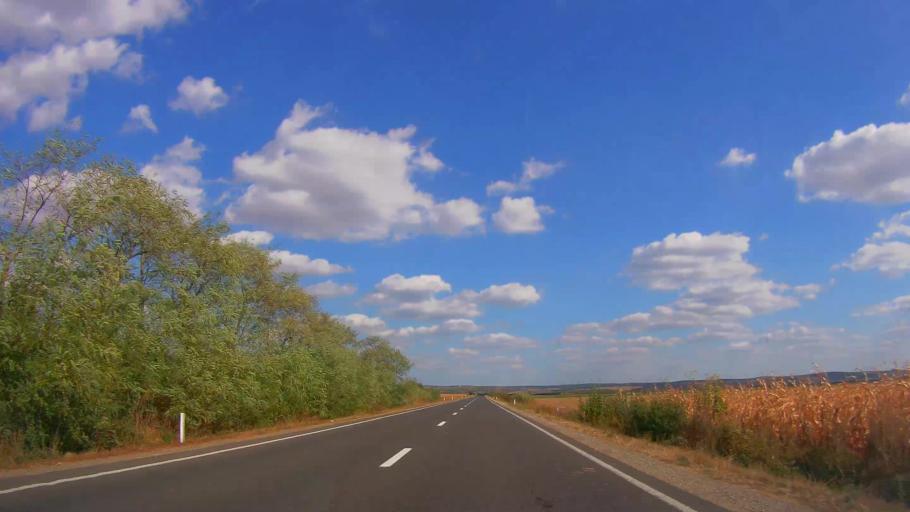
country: RO
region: Satu Mare
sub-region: Comuna Acas
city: Acas
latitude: 47.5400
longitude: 22.7967
